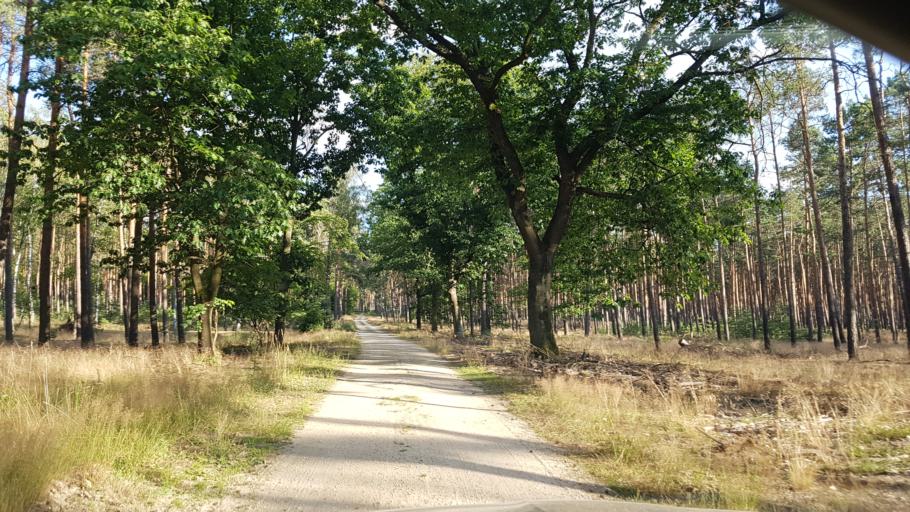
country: DE
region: Brandenburg
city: Trobitz
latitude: 51.6276
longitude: 13.4097
